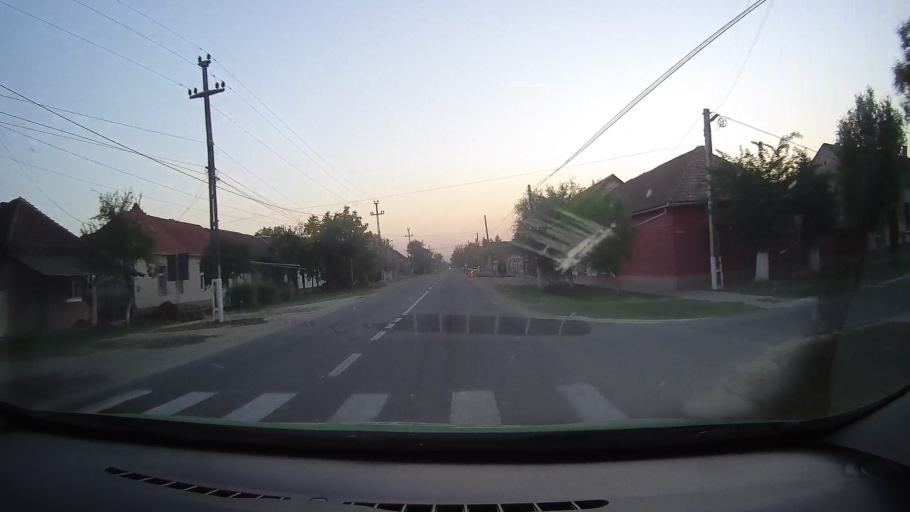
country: RO
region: Arad
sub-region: Comuna Santana
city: Santana
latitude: 46.3422
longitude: 21.4971
